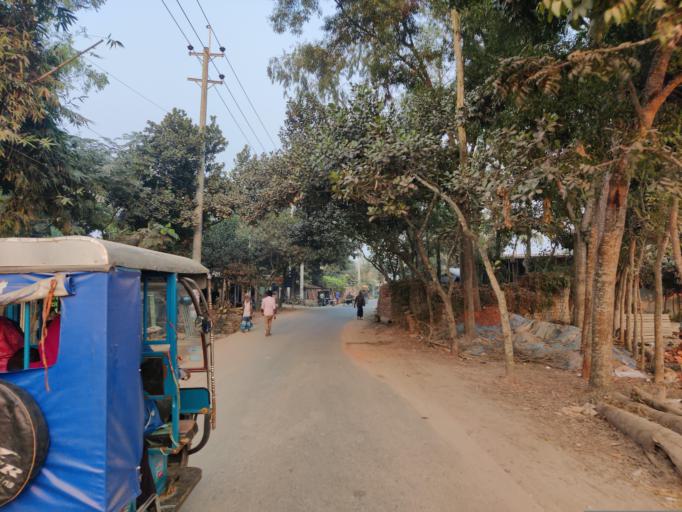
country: BD
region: Dhaka
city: Bajitpur
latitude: 24.1591
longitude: 90.8083
